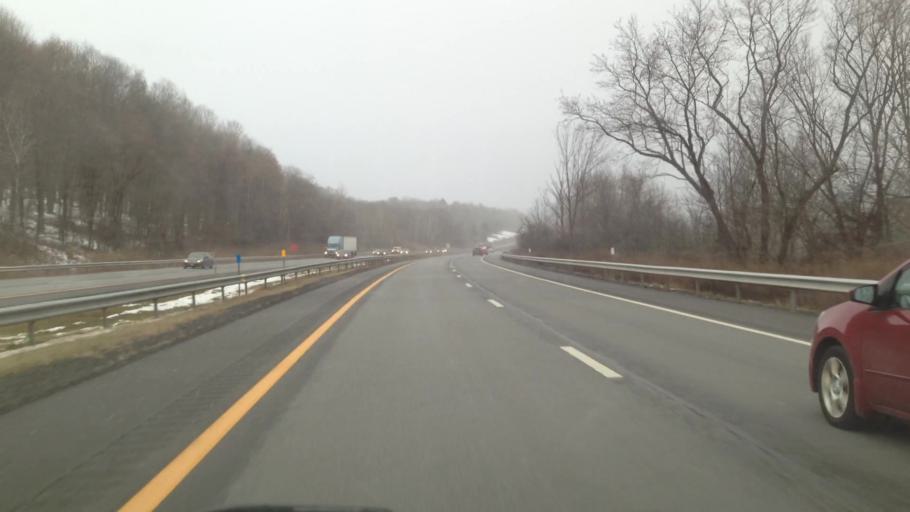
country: US
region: New York
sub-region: Schenectady County
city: Scotia
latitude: 42.8747
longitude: -74.0580
